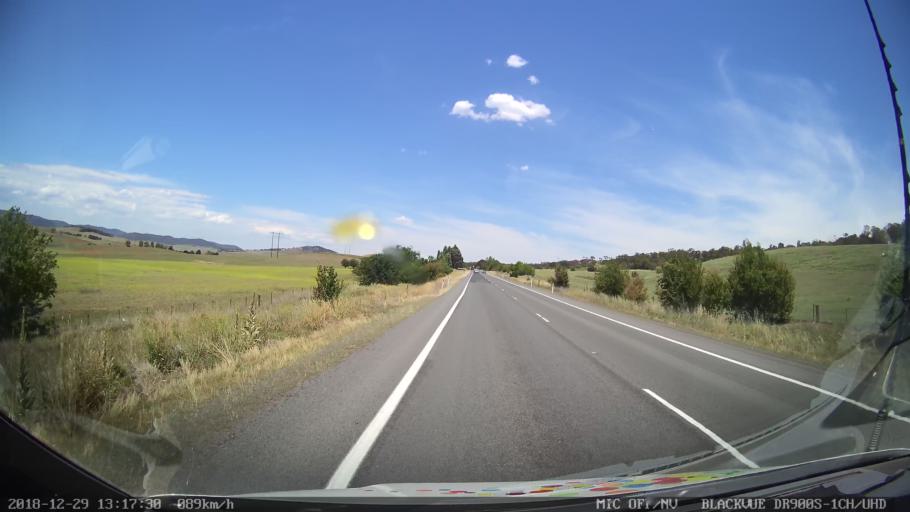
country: AU
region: Australian Capital Territory
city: Macarthur
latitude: -35.7383
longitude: 149.1607
